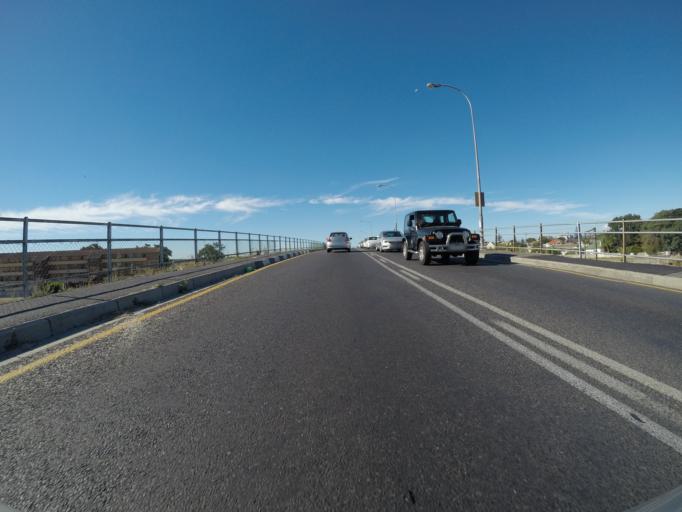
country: ZA
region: Western Cape
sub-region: City of Cape Town
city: Kraaifontein
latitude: -33.9326
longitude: 18.6758
